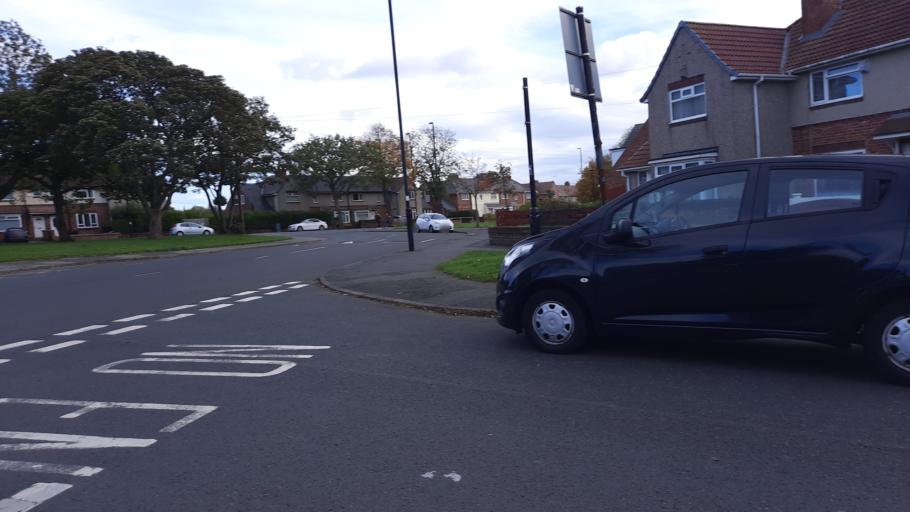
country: GB
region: England
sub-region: Borough of North Tyneside
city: North Shields
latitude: 55.0088
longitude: -1.4685
